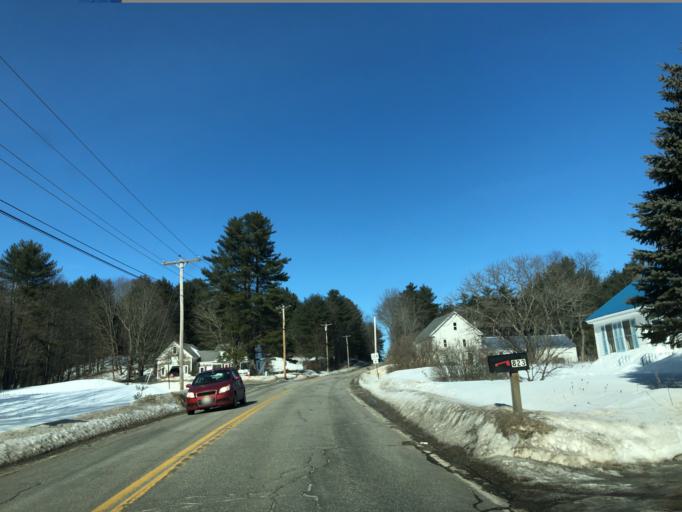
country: US
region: Maine
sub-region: Oxford County
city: Hebron
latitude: 44.1746
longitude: -70.3673
